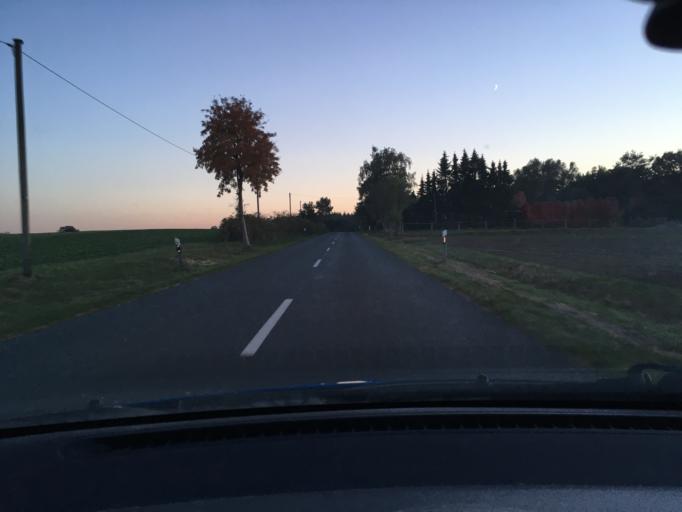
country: DE
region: Lower Saxony
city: Reinstorf
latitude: 53.2276
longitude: 10.5708
